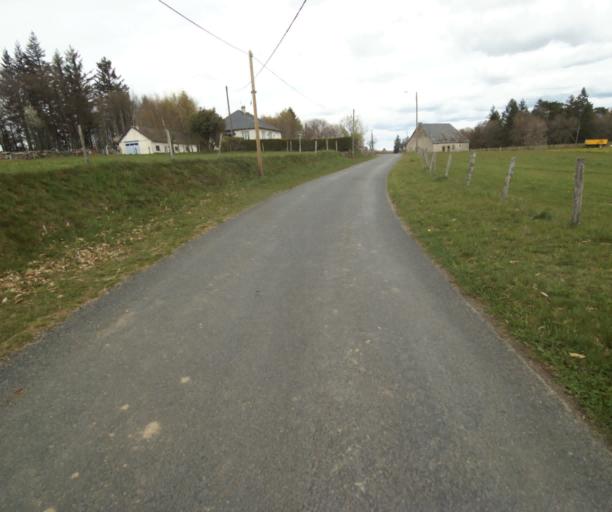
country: FR
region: Limousin
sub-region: Departement de la Correze
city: Laguenne
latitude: 45.2059
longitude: 1.8821
